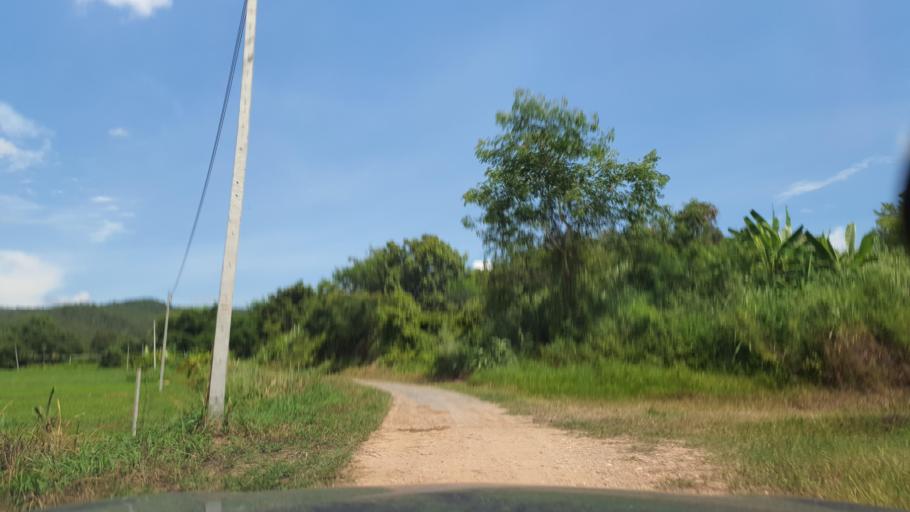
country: TH
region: Chiang Mai
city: Mae On
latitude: 18.7839
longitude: 99.1973
